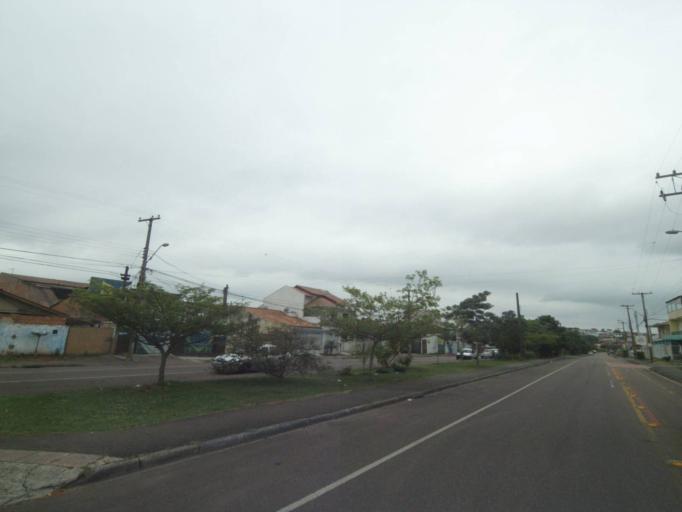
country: BR
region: Parana
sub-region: Sao Jose Dos Pinhais
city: Sao Jose dos Pinhais
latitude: -25.5367
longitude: -49.2554
